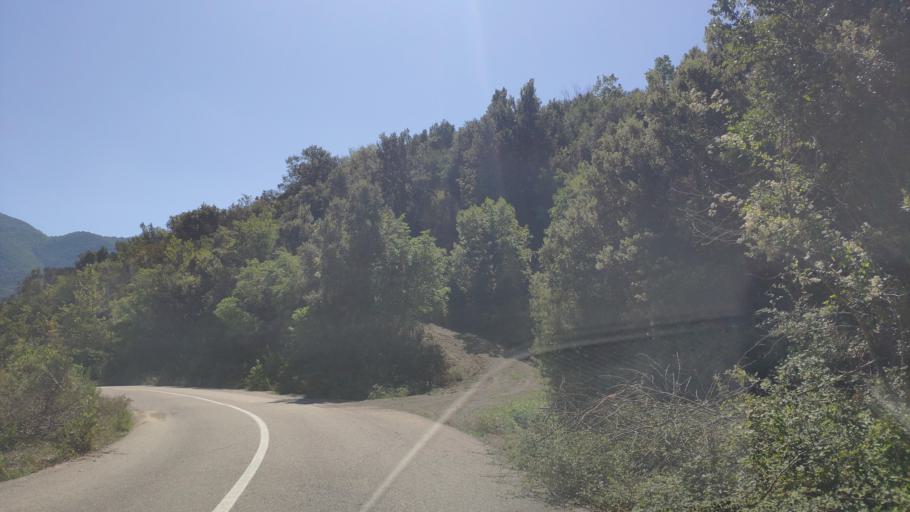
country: GR
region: Central Greece
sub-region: Nomos Evrytanias
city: Kerasochori
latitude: 39.0002
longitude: 21.5484
